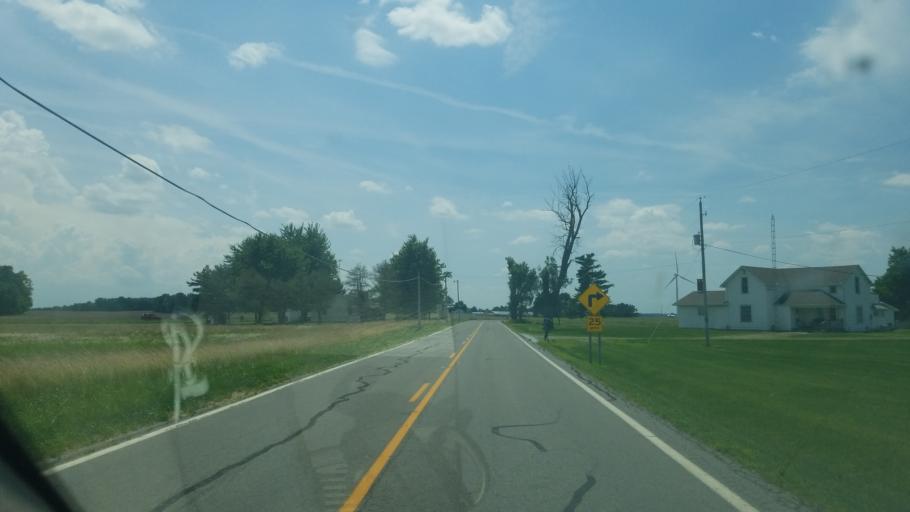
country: US
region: Ohio
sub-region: Hardin County
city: Ada
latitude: 40.7777
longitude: -83.7020
